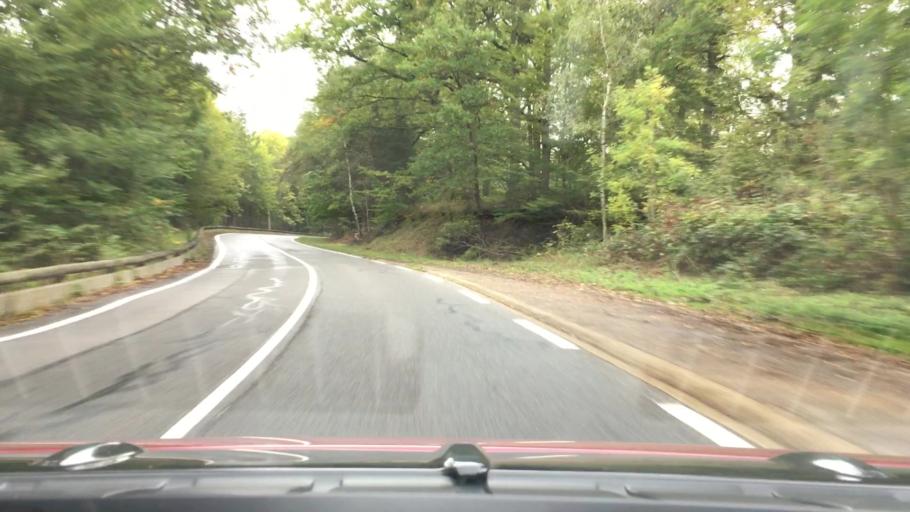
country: FR
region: Ile-de-France
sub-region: Departement des Yvelines
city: Saint-Leger-en-Yvelines
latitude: 48.7400
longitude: 1.7771
